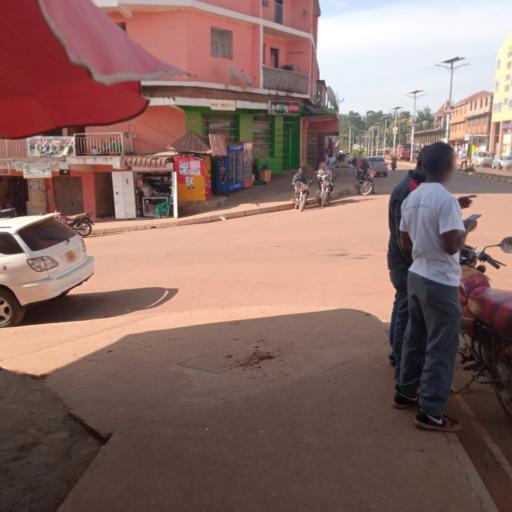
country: UG
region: Central Region
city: Masaka
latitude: -0.3457
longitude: 31.7381
